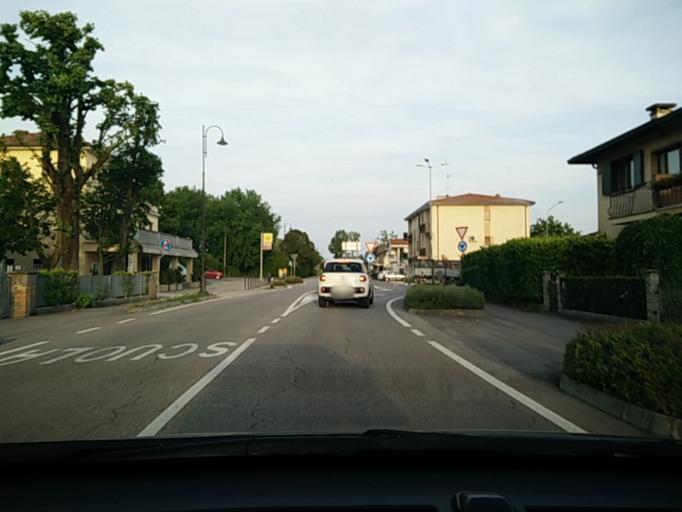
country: IT
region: Veneto
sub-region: Provincia di Venezia
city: Meolo
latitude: 45.5597
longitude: 12.4348
